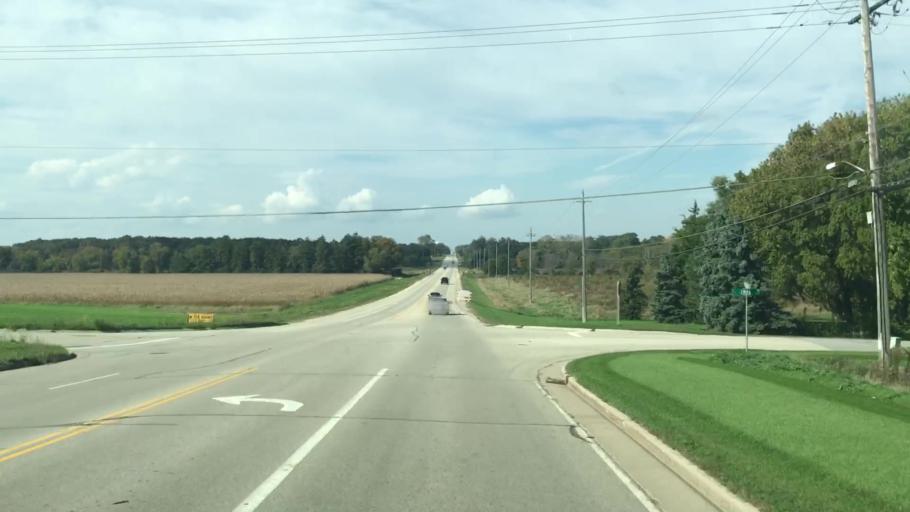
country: US
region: Wisconsin
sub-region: Ozaukee County
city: Mequon
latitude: 43.2216
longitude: -88.0232
